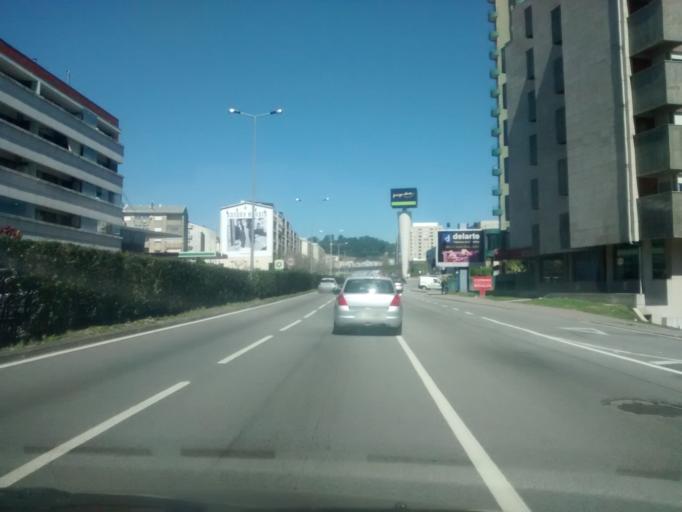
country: PT
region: Braga
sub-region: Braga
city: Braga
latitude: 41.5548
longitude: -8.4070
